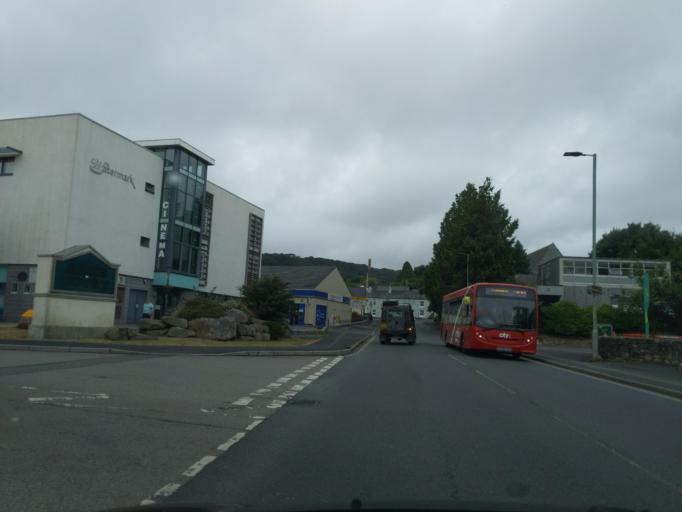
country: GB
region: England
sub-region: Devon
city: Ivybridge
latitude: 50.3893
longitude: -3.9186
